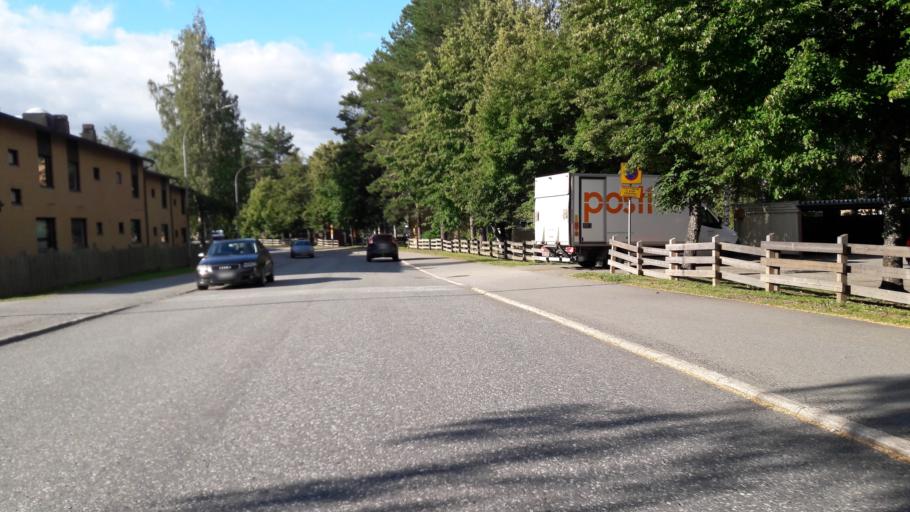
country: FI
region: North Karelia
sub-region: Joensuu
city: Joensuu
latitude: 62.6032
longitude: 29.8000
